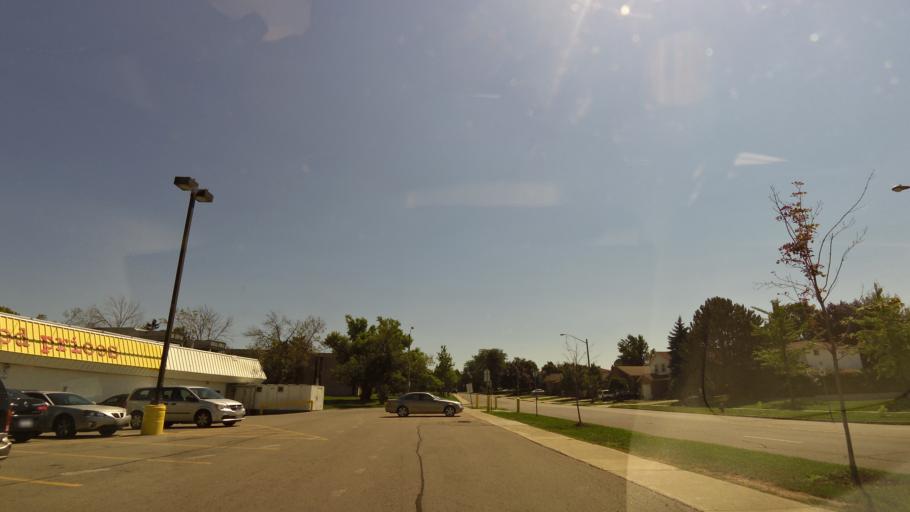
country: CA
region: Ontario
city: Ancaster
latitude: 43.2332
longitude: -79.9242
